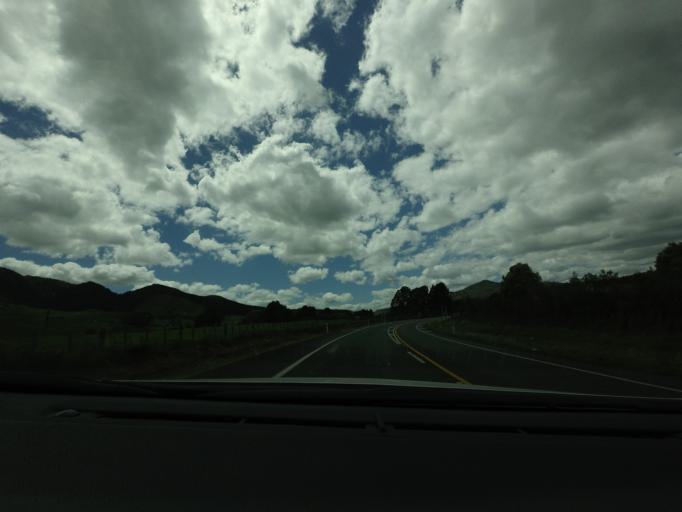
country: NZ
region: Bay of Plenty
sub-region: Rotorua District
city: Rotorua
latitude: -38.3433
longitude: 176.3611
